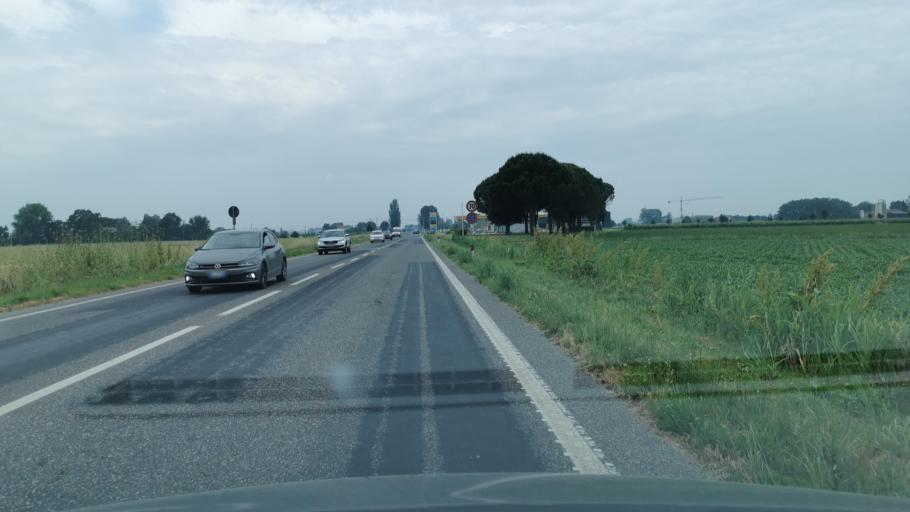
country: IT
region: Emilia-Romagna
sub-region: Provincia di Ravenna
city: Godo
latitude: 44.3937
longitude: 12.0657
